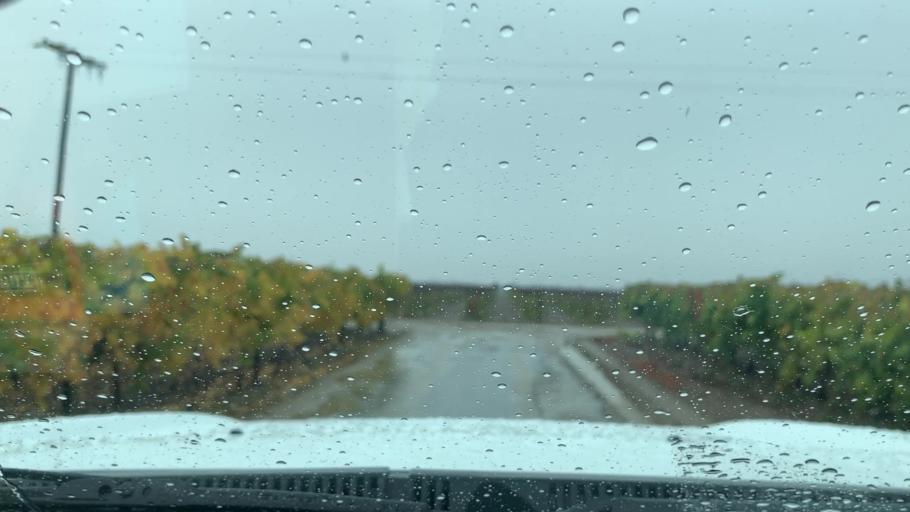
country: US
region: California
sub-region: Tulare County
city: Richgrove
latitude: 35.8378
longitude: -119.1698
